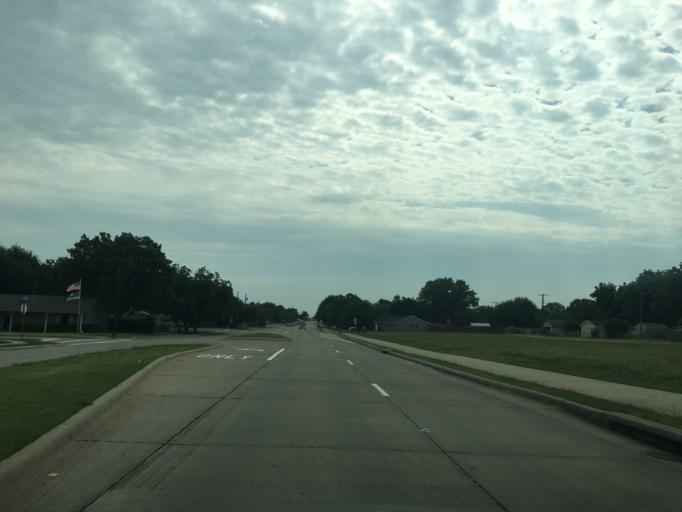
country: US
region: Texas
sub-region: Collin County
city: Wylie
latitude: 33.0062
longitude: -96.5386
